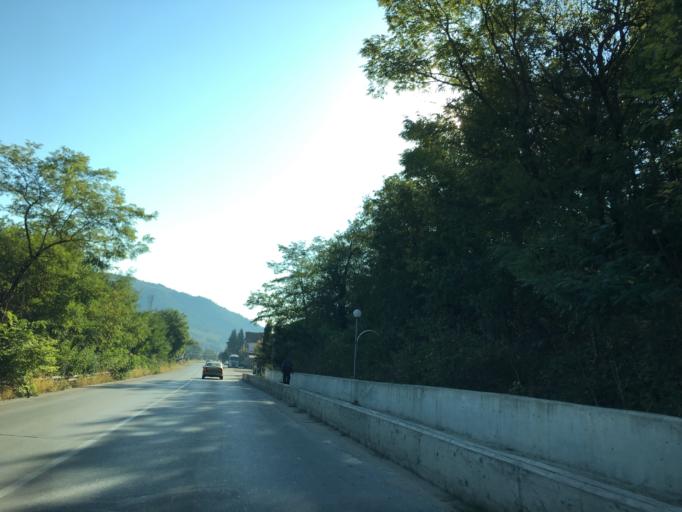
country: BG
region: Pazardzhik
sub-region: Obshtina Belovo
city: Belovo
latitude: 42.2288
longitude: 23.9708
